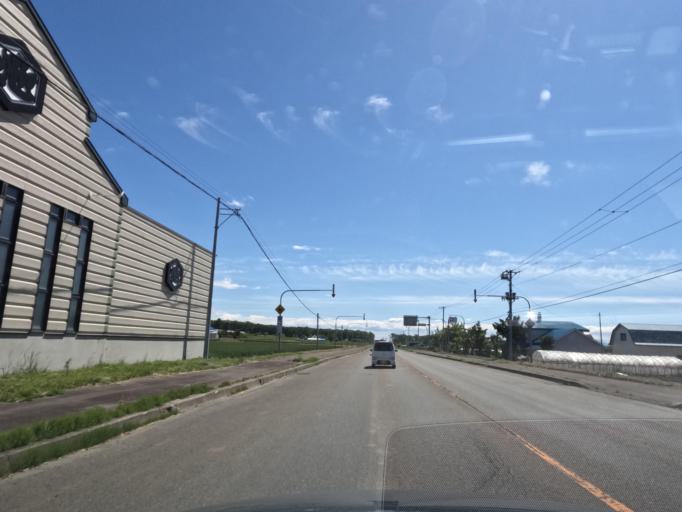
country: JP
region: Hokkaido
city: Iwamizawa
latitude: 43.0581
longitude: 141.7326
